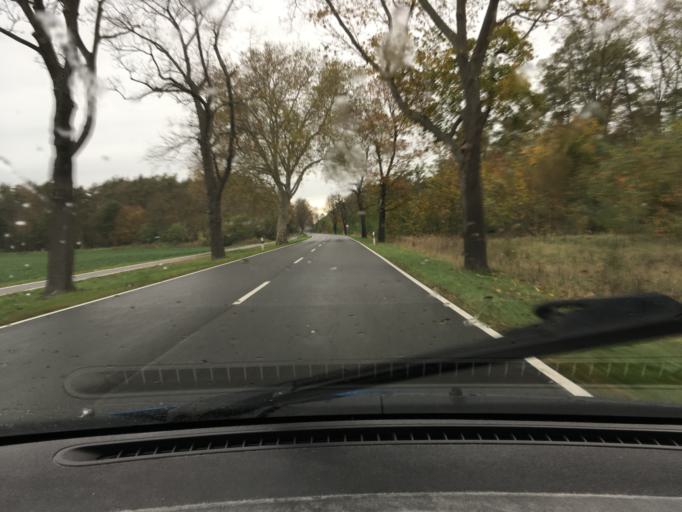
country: DE
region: Saxony-Anhalt
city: Rodleben
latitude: 51.9097
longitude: 12.1971
